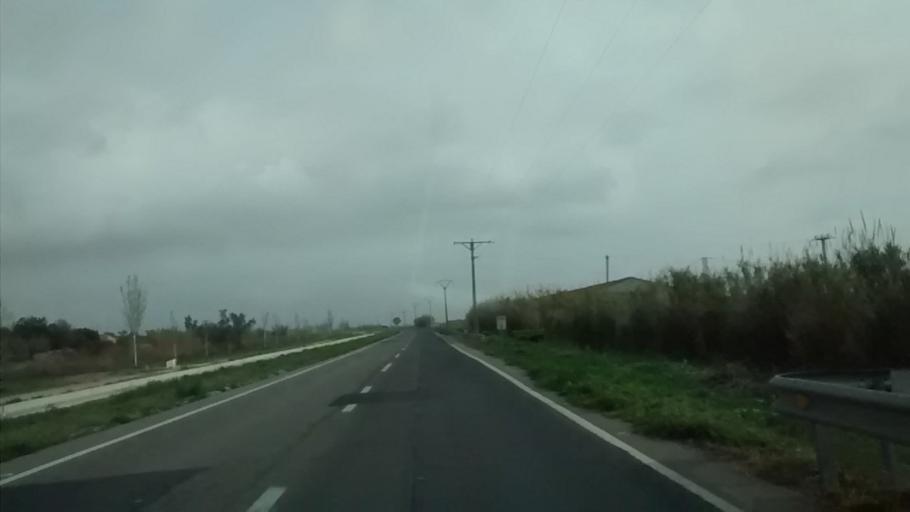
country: ES
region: Catalonia
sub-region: Provincia de Tarragona
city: Sant Carles de la Rapita
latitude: 40.6293
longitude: 0.6008
